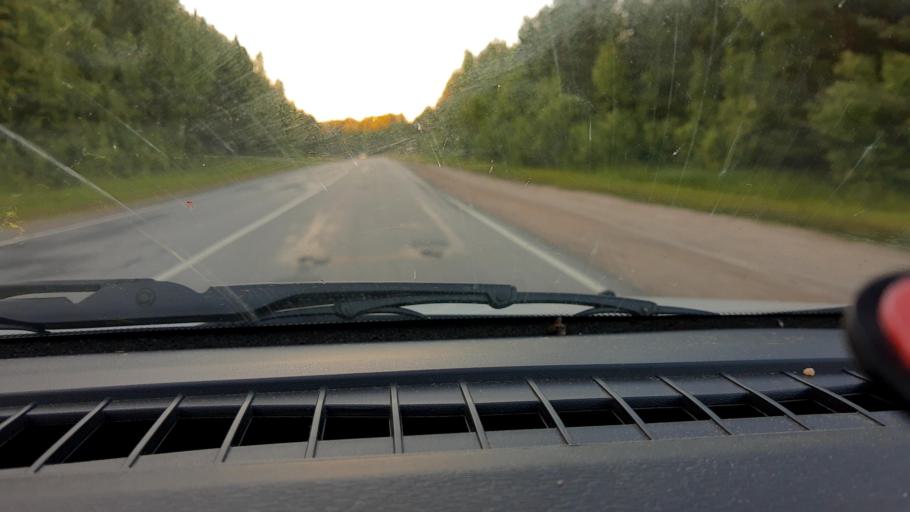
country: RU
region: Nizjnij Novgorod
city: Krasnyye Baki
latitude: 56.9827
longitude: 45.1167
